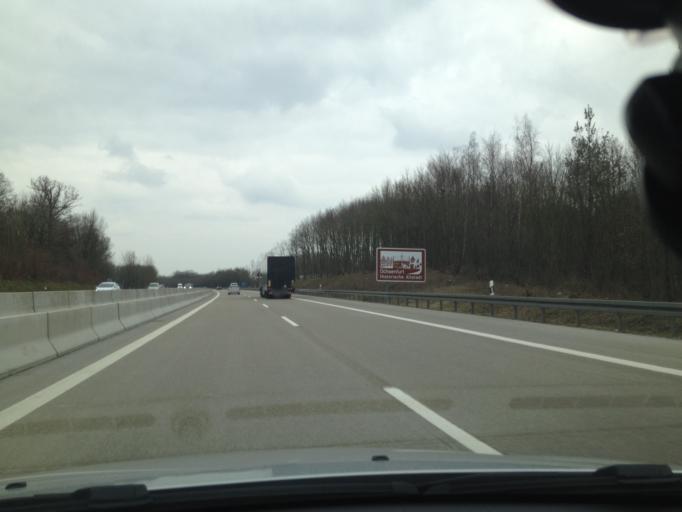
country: DE
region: Bavaria
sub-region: Regierungsbezirk Unterfranken
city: Martinsheim
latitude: 49.6235
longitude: 10.1751
